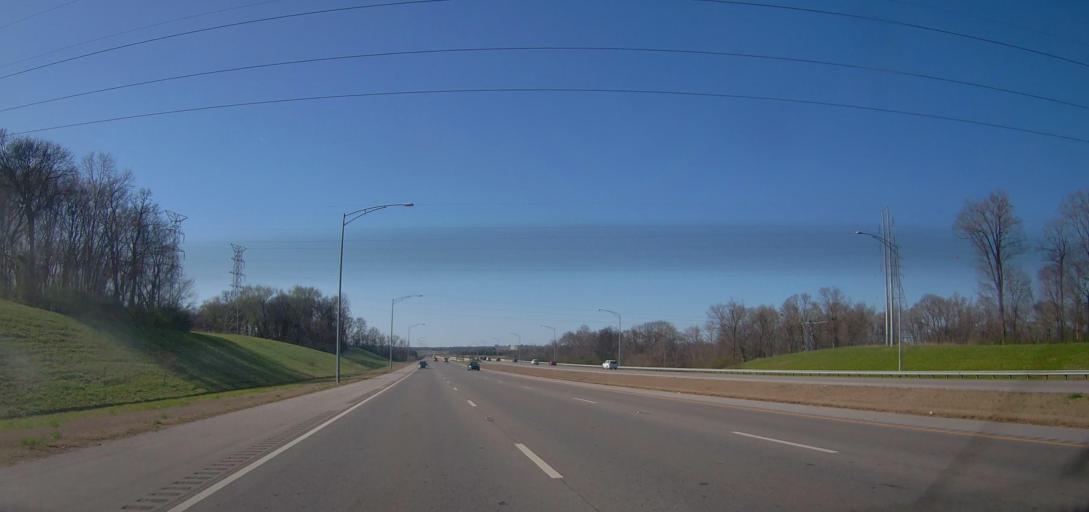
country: US
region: Alabama
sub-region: Lauderdale County
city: East Florence
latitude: 34.7879
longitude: -87.6394
